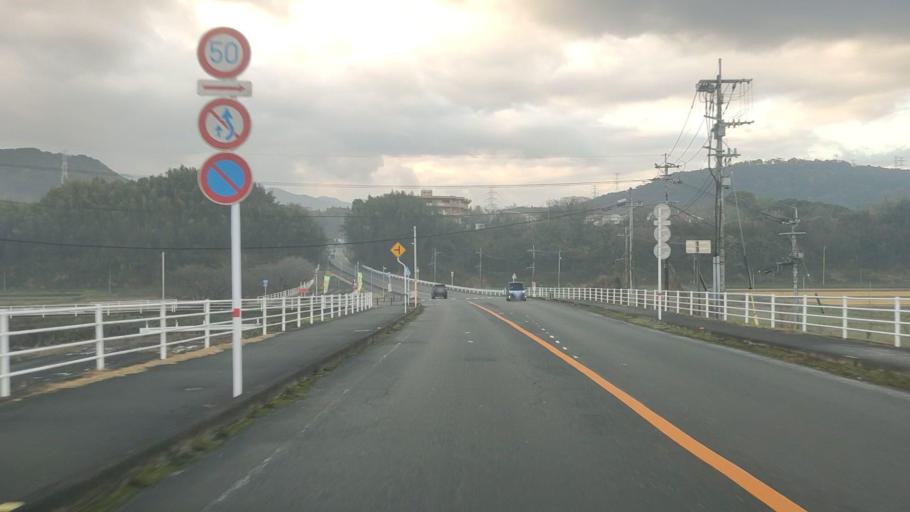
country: JP
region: Kumamoto
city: Matsubase
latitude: 32.6416
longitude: 130.8129
